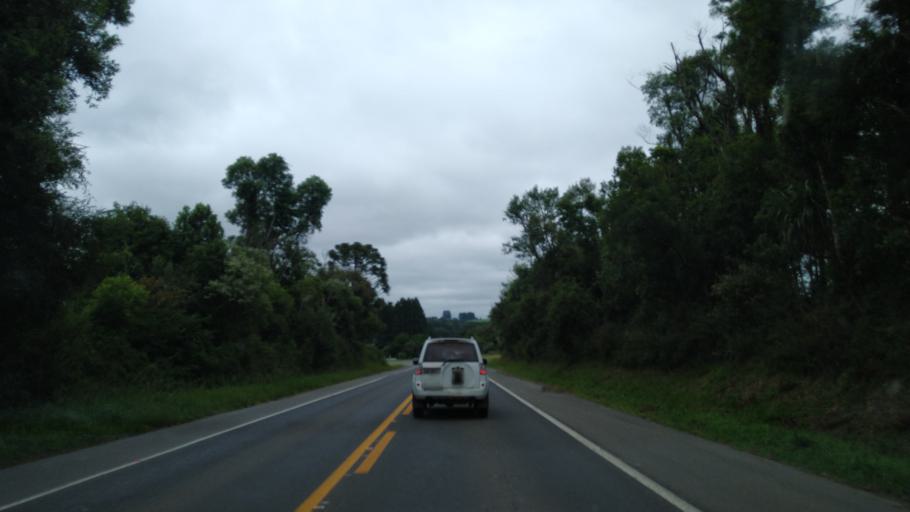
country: BR
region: Santa Catarina
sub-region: Tres Barras
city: Tres Barras
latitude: -26.1813
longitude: -50.1988
